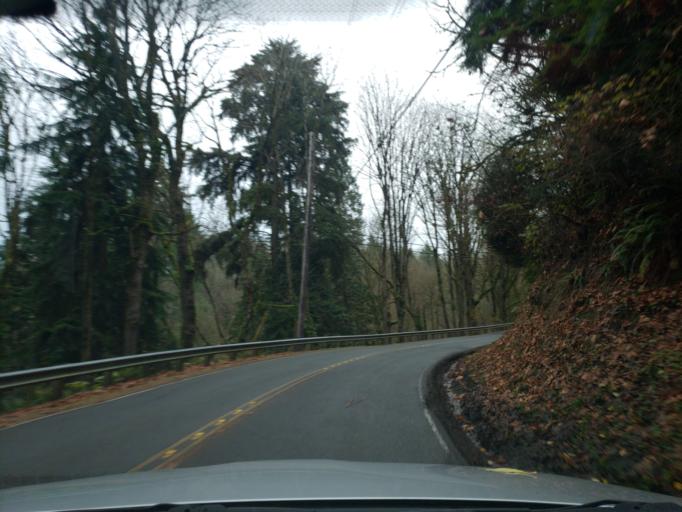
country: US
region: Washington
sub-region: King County
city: Bothell
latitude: 47.7514
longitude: -122.1937
